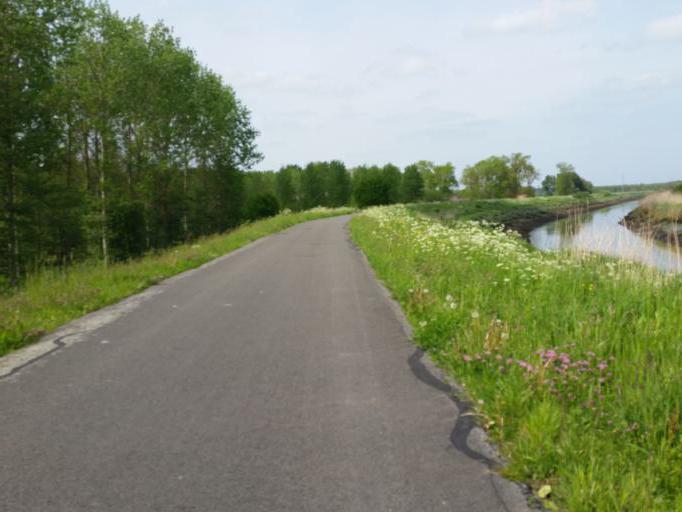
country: BE
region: Flanders
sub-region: Provincie Antwerpen
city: Rumst
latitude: 51.0560
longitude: 4.4279
